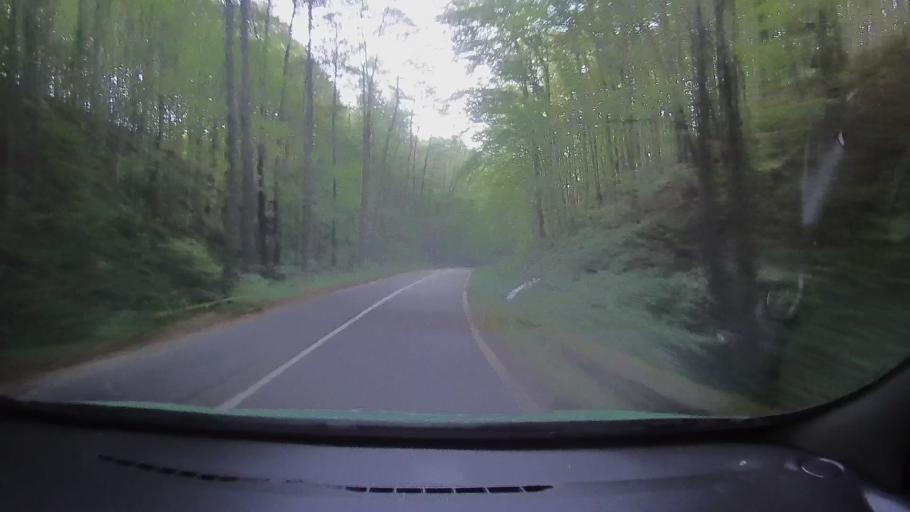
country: RO
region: Timis
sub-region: Comuna Nadrag
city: Nadrag
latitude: 45.6835
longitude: 22.1566
